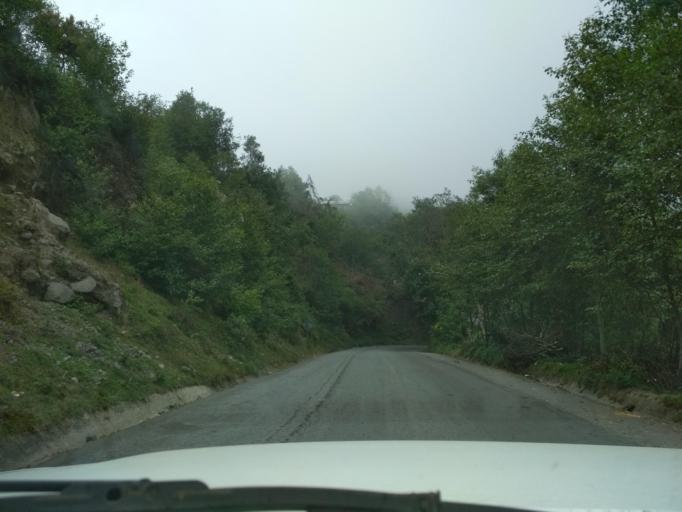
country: MX
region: Veracruz
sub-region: Mariano Escobedo
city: San Isidro el Berro
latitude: 18.9479
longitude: -97.1995
